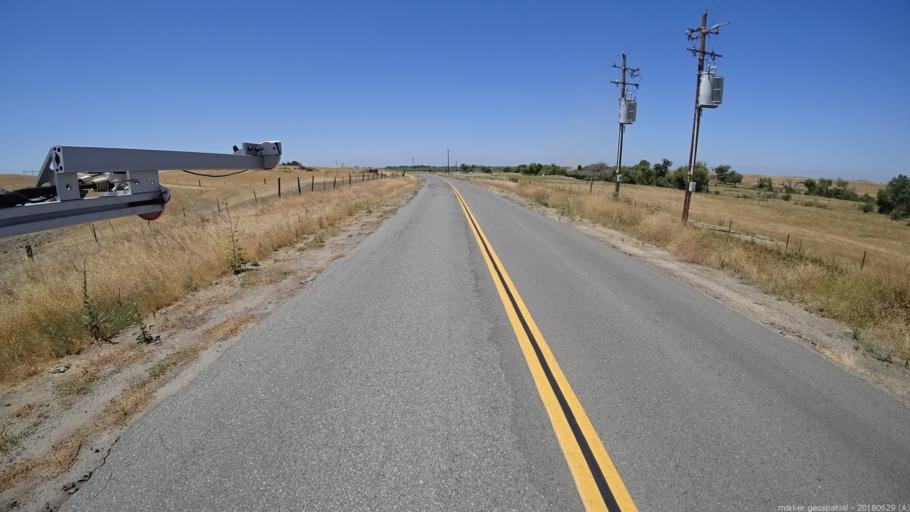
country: US
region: California
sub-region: Madera County
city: Bonadelle Ranchos-Madera Ranchos
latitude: 37.0705
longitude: -119.9068
